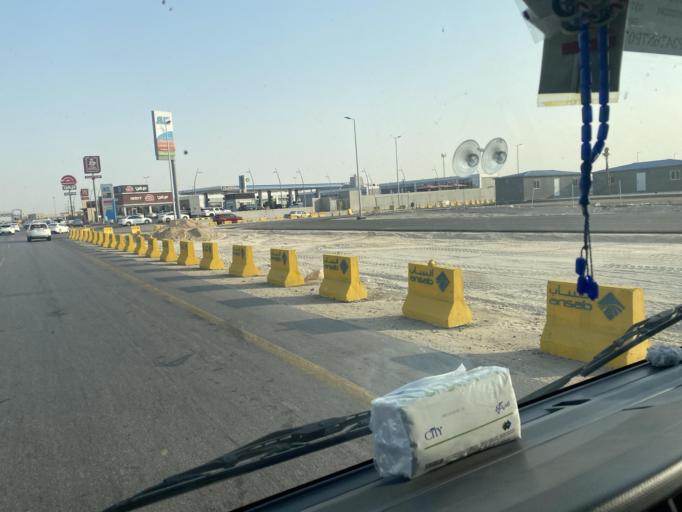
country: SA
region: Eastern Province
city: Sayhat
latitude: 26.4081
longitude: 50.0142
